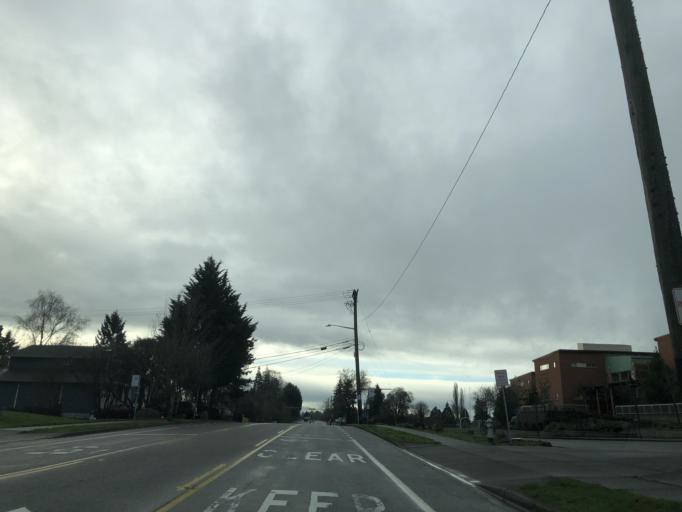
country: US
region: Washington
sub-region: Pierce County
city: Tacoma
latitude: 47.2125
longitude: -122.4582
